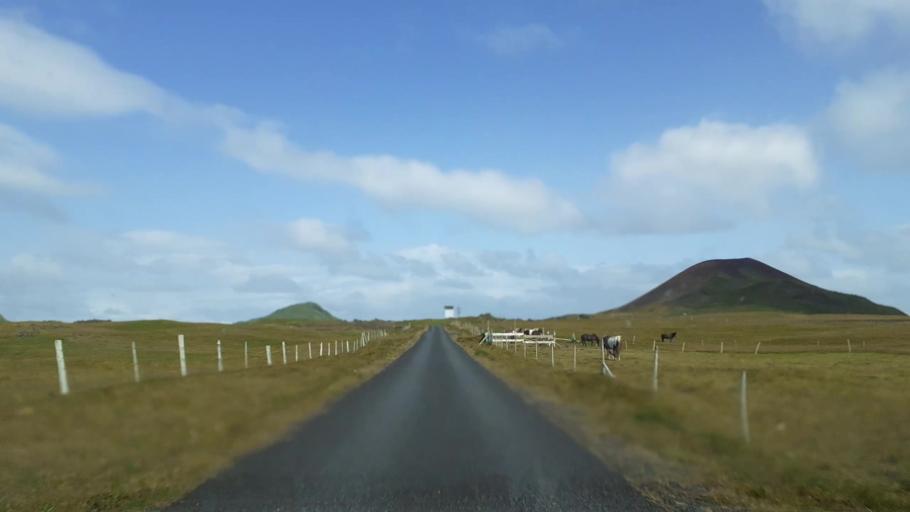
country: IS
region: South
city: Vestmannaeyjar
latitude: 63.4215
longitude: -20.2787
